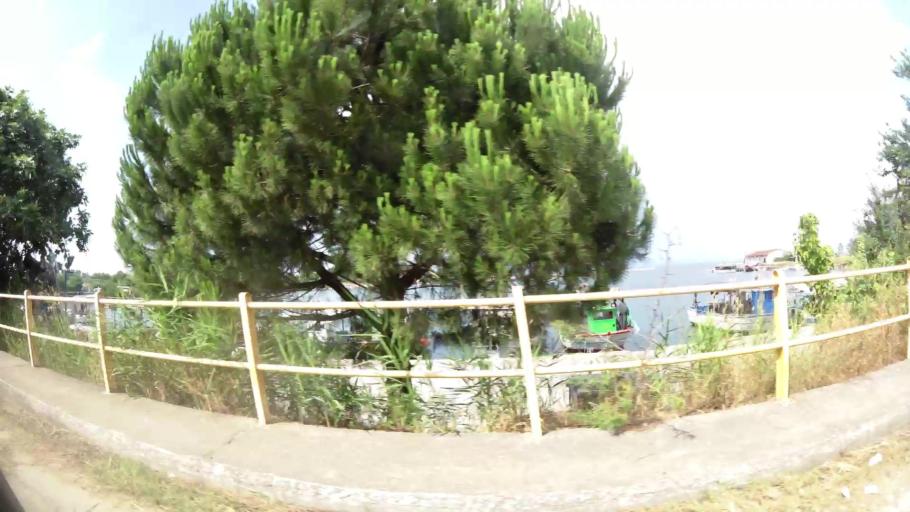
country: GR
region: Central Macedonia
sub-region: Nomos Pierias
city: Makrygialos
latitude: 40.3762
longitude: 22.6245
